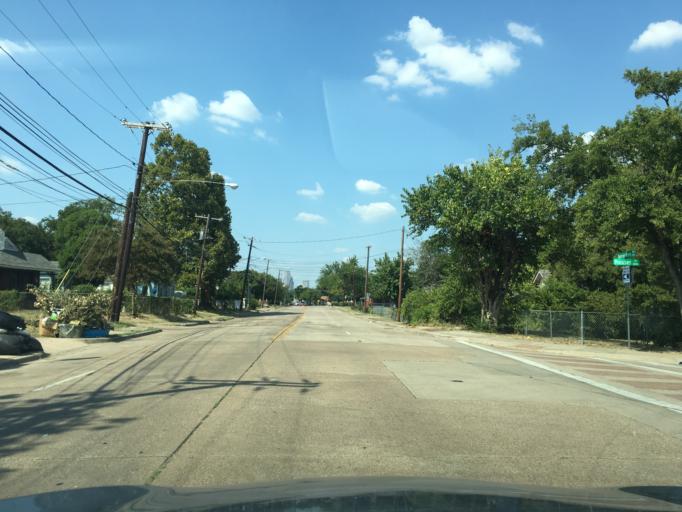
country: US
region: Texas
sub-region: Dallas County
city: Dallas
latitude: 32.7376
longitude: -96.7937
